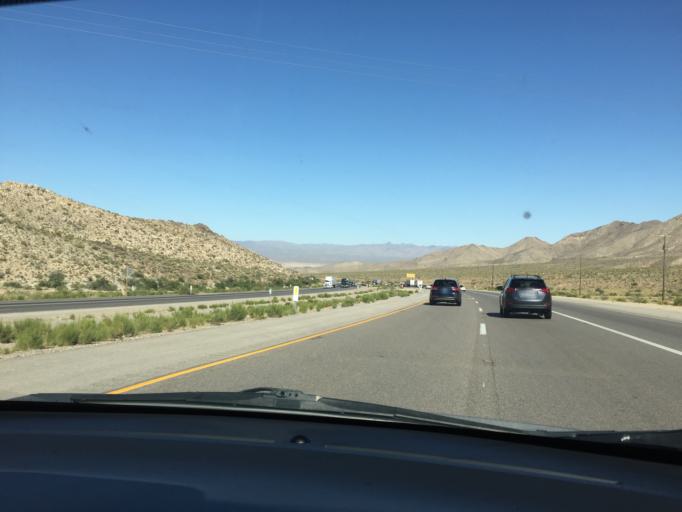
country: US
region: Nevada
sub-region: Clark County
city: Sandy Valley
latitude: 35.4623
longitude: -115.4781
